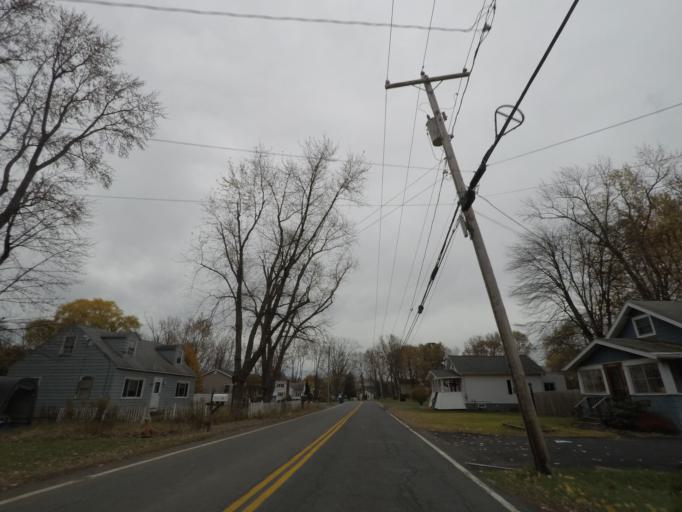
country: US
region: New York
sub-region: Albany County
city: Cohoes
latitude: 42.7955
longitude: -73.7259
